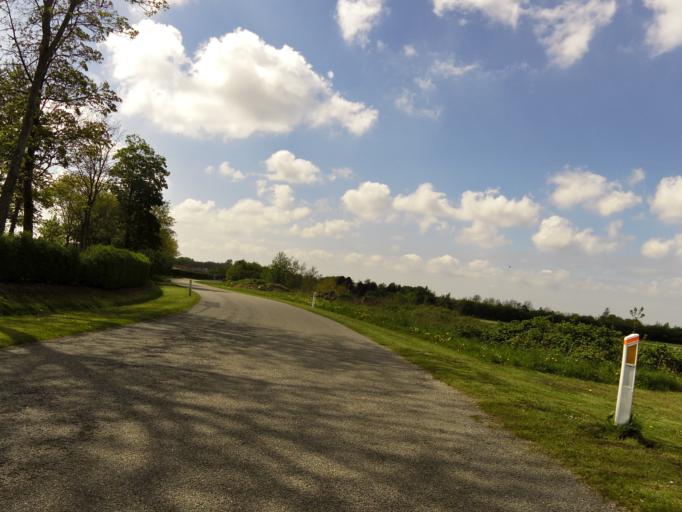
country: DK
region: South Denmark
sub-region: Tonder Kommune
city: Toftlund
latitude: 55.1826
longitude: 9.0897
